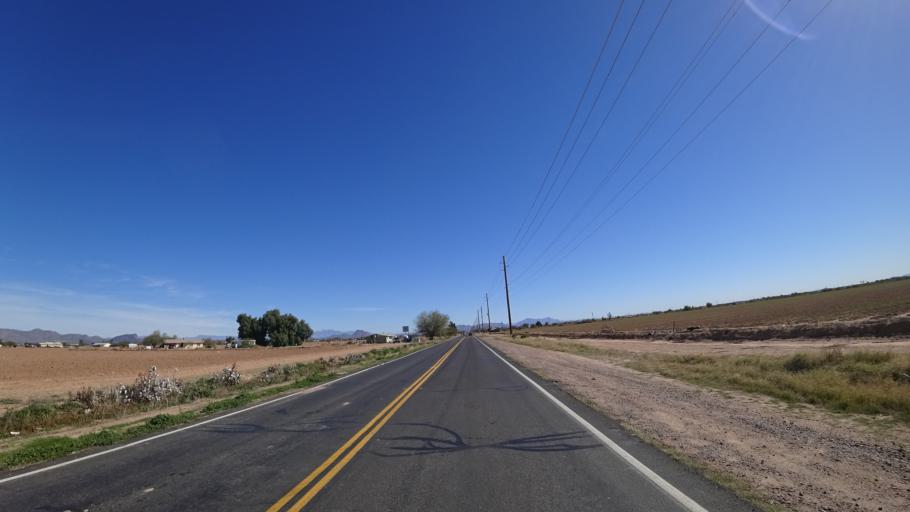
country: US
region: Arizona
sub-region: Maricopa County
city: Scottsdale
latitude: 33.4950
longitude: -111.8651
